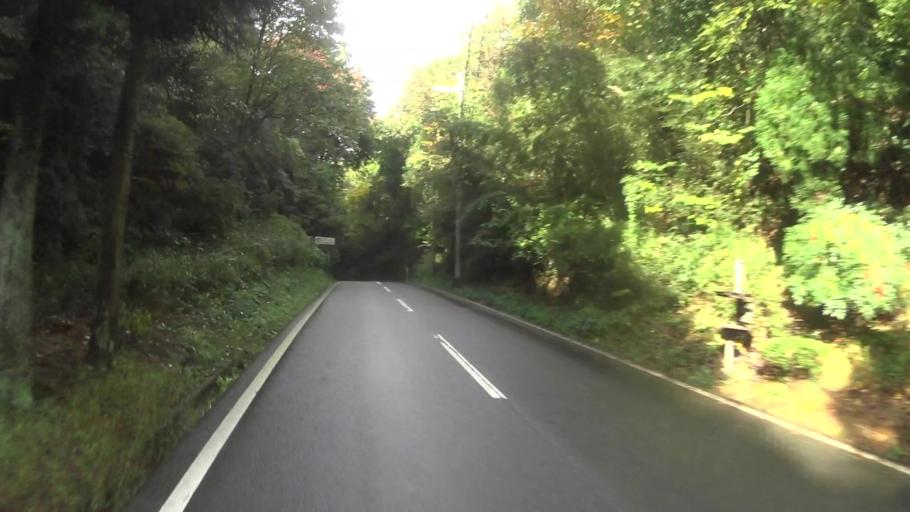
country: JP
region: Kyoto
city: Ayabe
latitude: 35.3718
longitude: 135.1903
